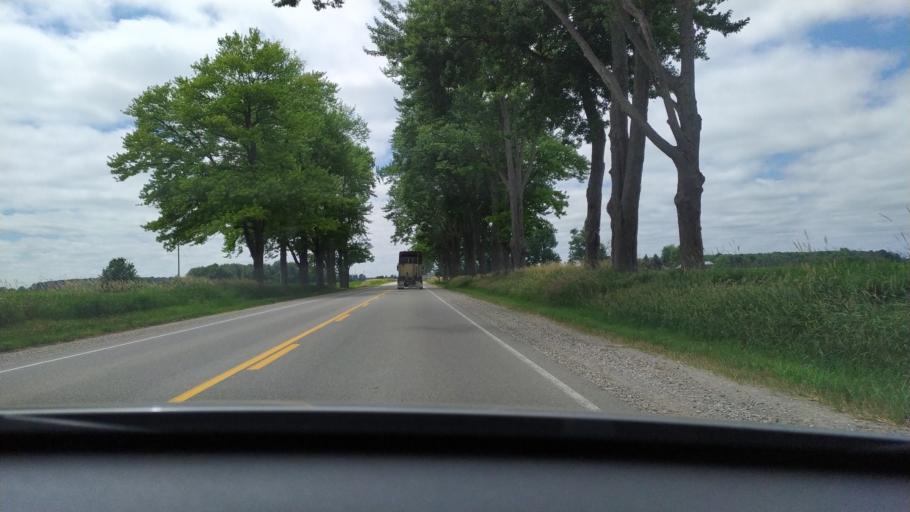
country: CA
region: Ontario
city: Stratford
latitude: 43.3159
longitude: -80.9646
